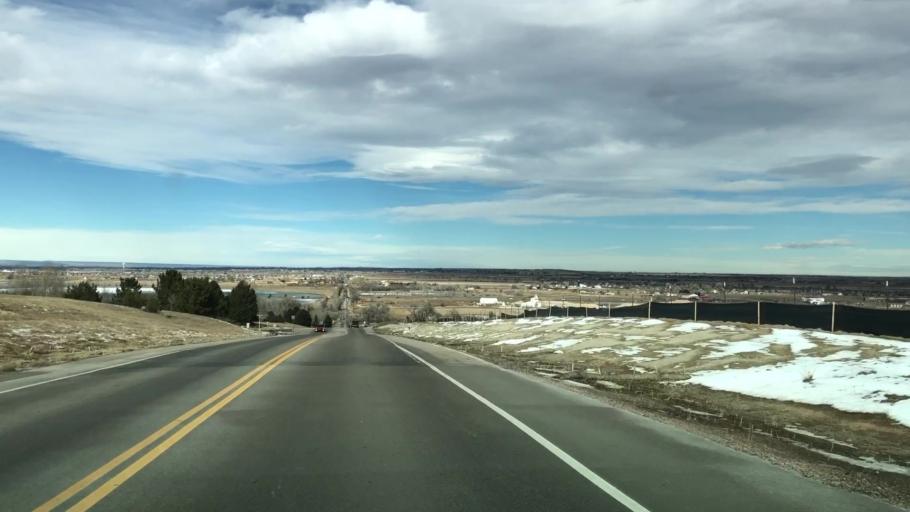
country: US
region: Colorado
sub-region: Weld County
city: Windsor
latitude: 40.4659
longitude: -104.9441
